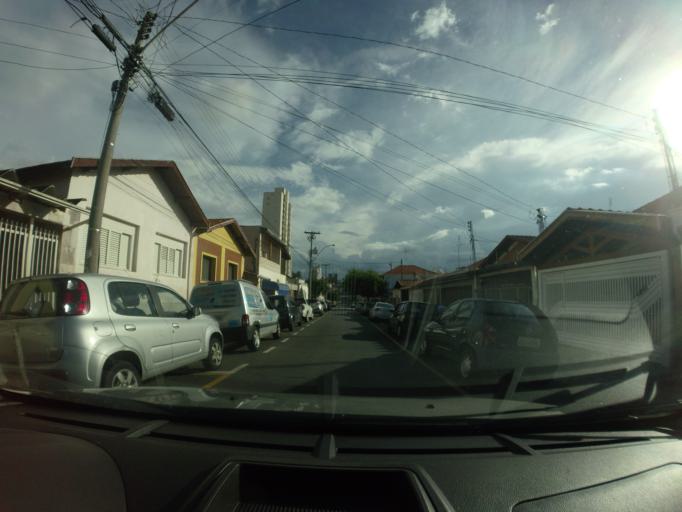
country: BR
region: Sao Paulo
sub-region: Piracicaba
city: Piracicaba
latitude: -22.7324
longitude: -47.6442
